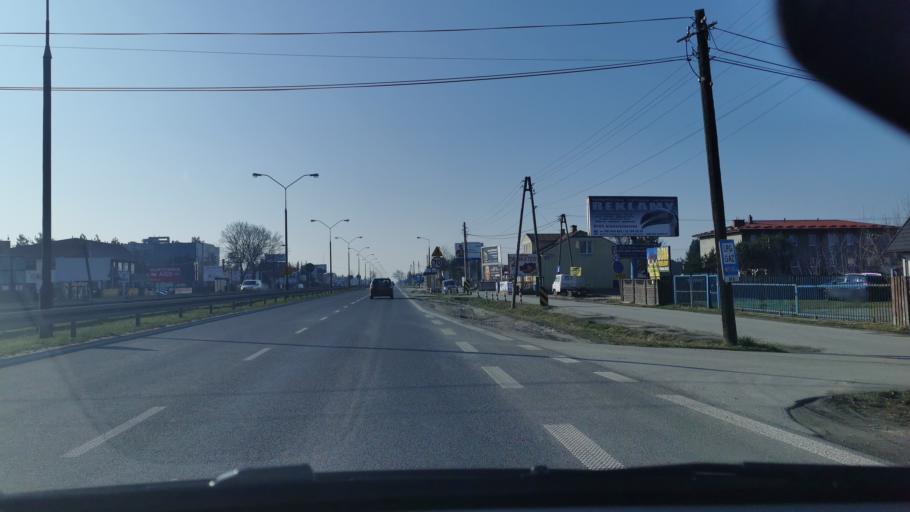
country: PL
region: Masovian Voivodeship
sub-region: Powiat pruszkowski
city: Nowe Grocholice
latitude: 52.1307
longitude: 20.8973
